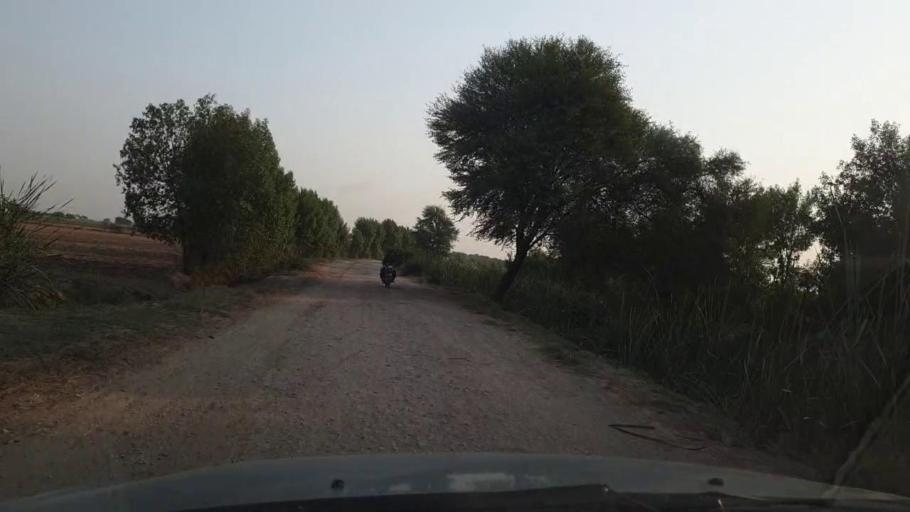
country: PK
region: Sindh
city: Tando Muhammad Khan
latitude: 25.0155
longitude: 68.4382
